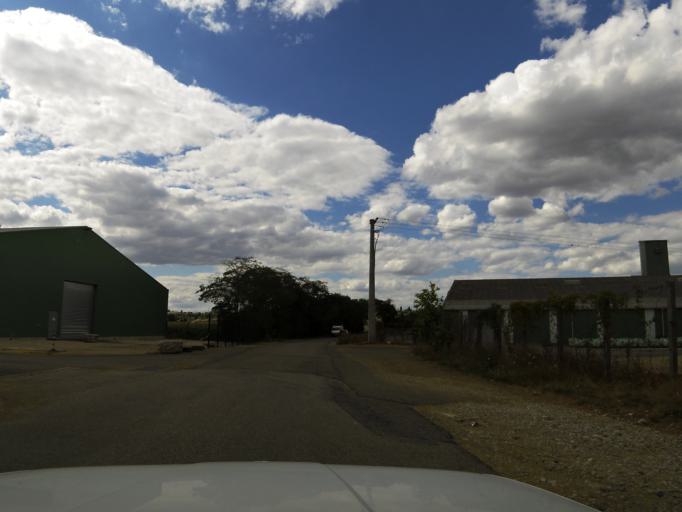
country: FR
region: Rhone-Alpes
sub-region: Departement de l'Ain
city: Meximieux
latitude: 45.8981
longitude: 5.2039
